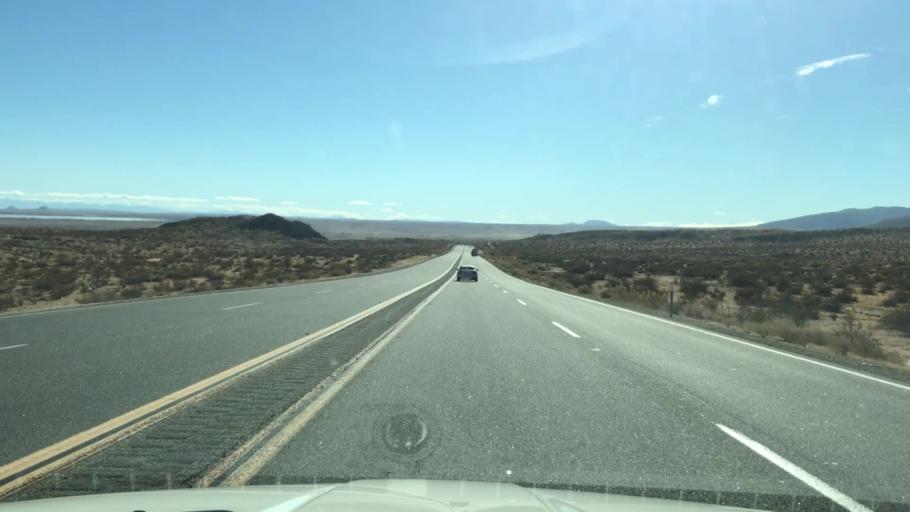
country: US
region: California
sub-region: Kern County
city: California City
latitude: 35.3296
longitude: -117.9756
